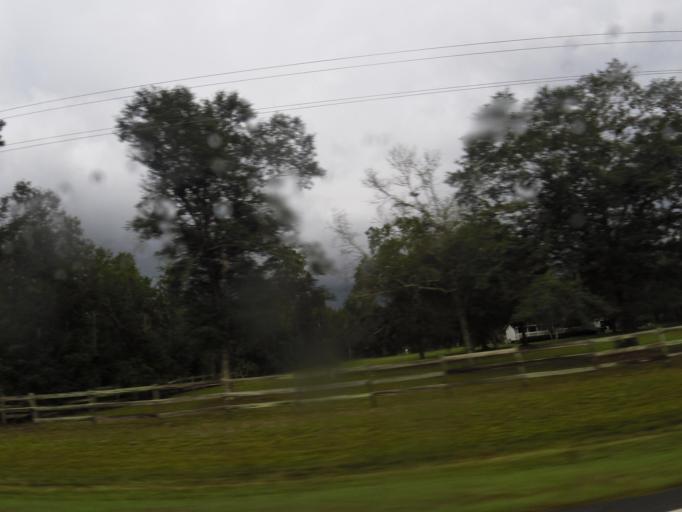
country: US
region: Florida
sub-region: Baker County
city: Macclenny
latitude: 30.3684
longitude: -82.1433
